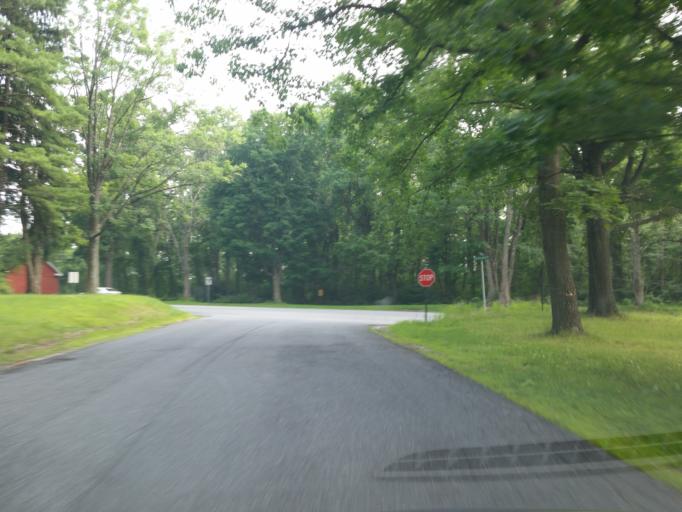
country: US
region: Pennsylvania
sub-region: Lebanon County
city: Jonestown
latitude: 40.4231
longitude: -76.5792
